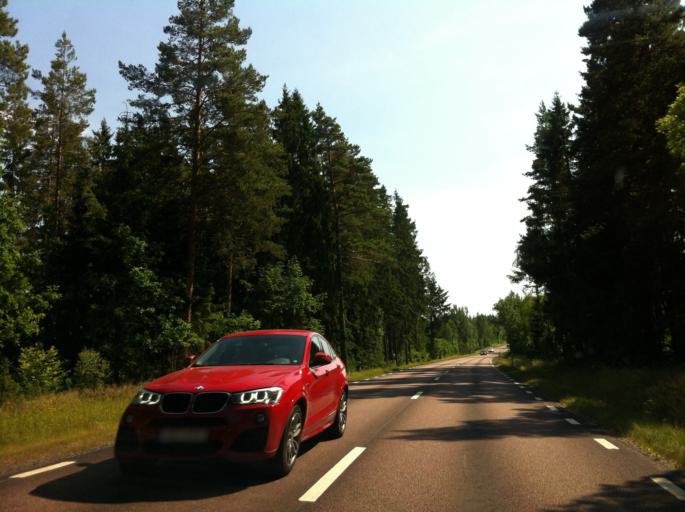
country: SE
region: Kalmar
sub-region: Nybro Kommun
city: Nybro
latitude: 56.8073
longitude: 15.7862
